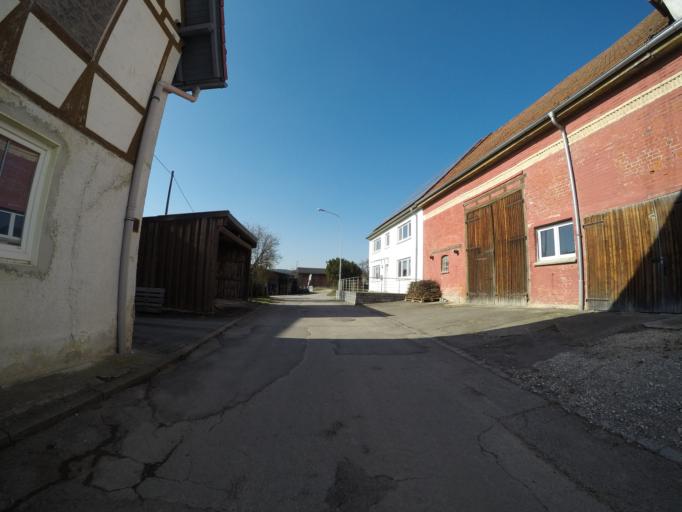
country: DE
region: Baden-Wuerttemberg
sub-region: Tuebingen Region
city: Erbach
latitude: 48.3884
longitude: 9.8590
